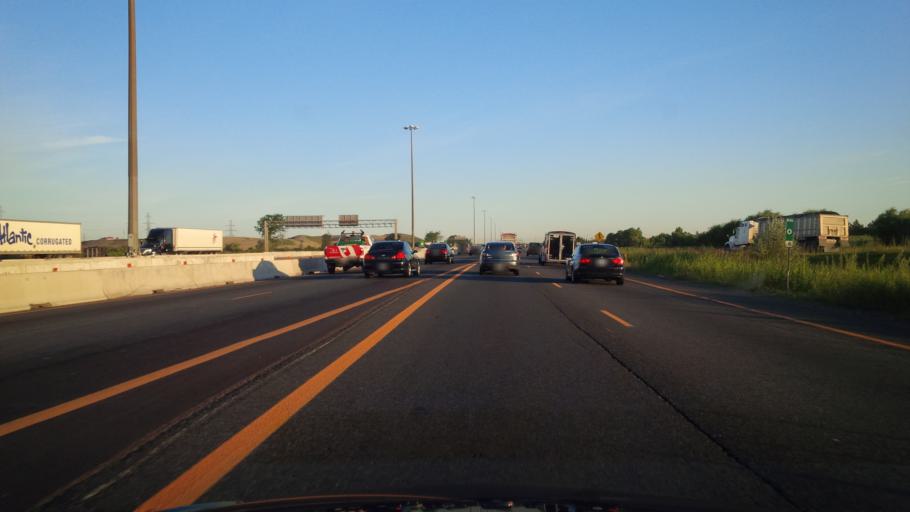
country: CA
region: Ontario
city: Mississauga
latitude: 43.6432
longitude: -79.6654
